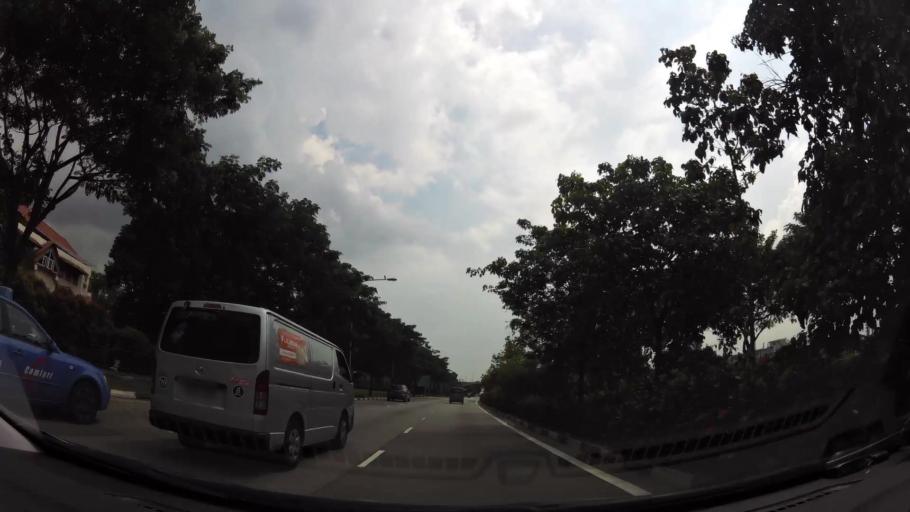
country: SG
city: Singapore
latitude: 1.2821
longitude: 103.7822
